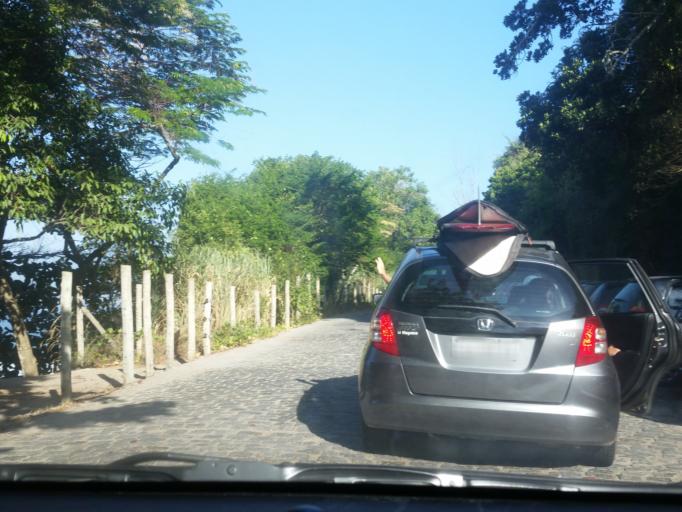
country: BR
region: Rio de Janeiro
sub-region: Nilopolis
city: Nilopolis
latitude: -23.0477
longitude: -43.5151
